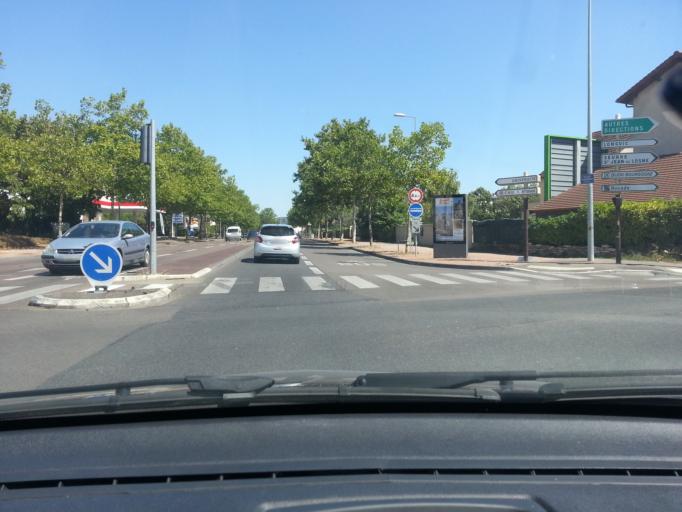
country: FR
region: Bourgogne
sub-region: Departement de la Cote-d'Or
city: Longvic
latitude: 47.3056
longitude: 5.0494
